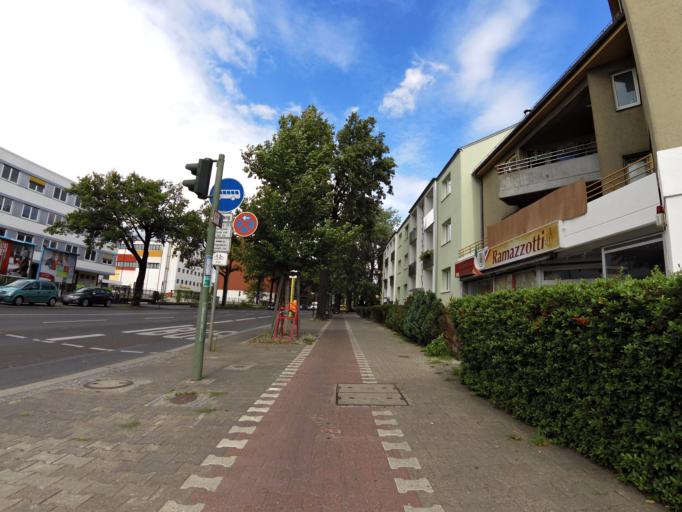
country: DE
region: Berlin
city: Mariendorf
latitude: 52.4349
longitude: 13.3785
